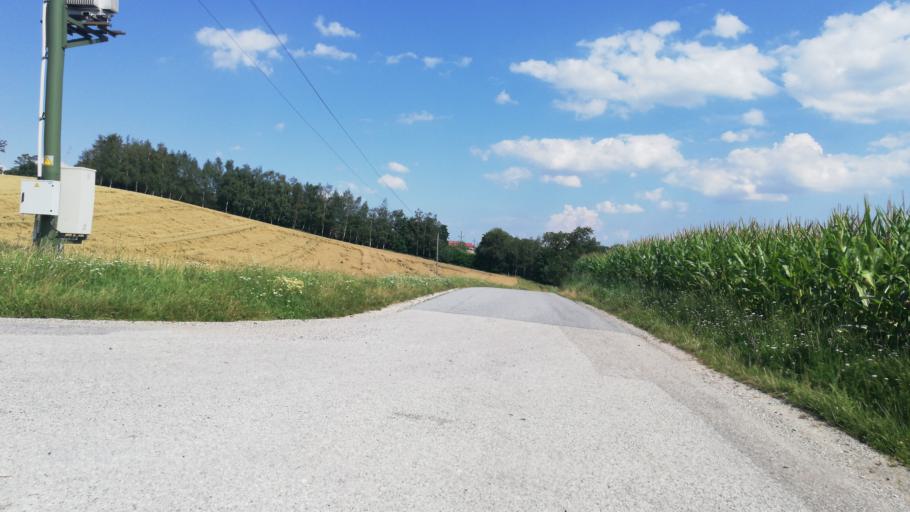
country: AT
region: Upper Austria
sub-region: Wels-Land
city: Pennewang
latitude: 48.1599
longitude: 13.8815
